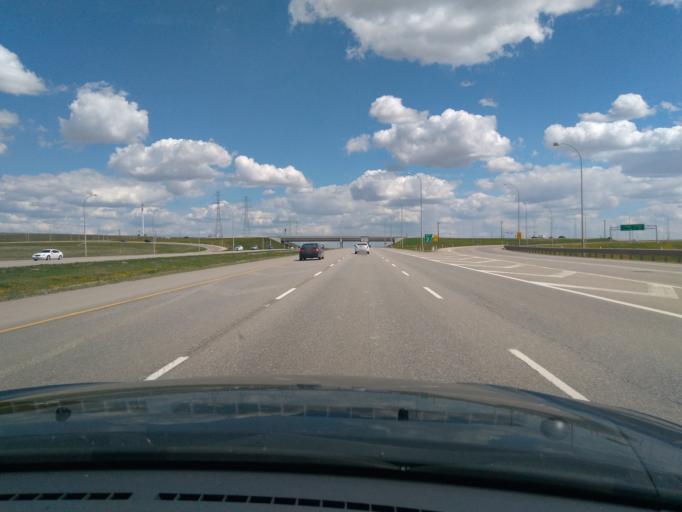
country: CA
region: Alberta
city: Calgary
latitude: 51.1738
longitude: -114.0760
